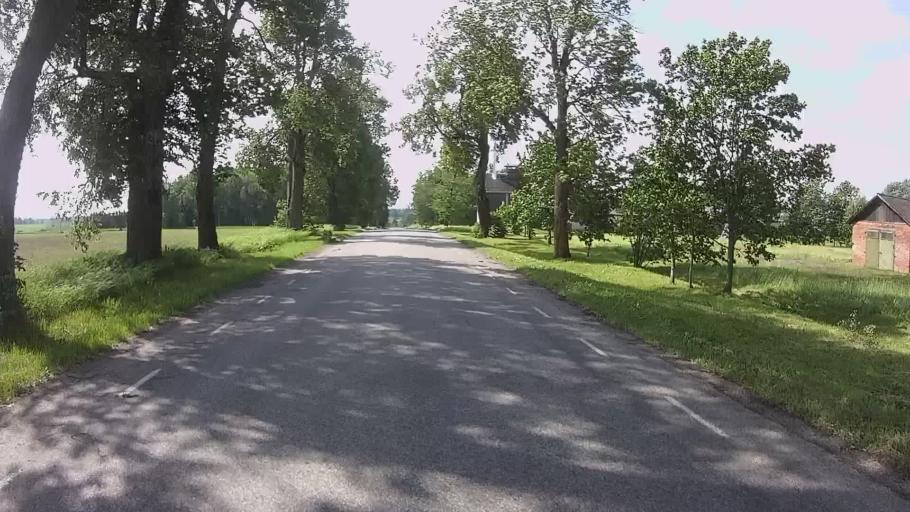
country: EE
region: Vorumaa
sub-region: Antsla vald
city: Vana-Antsla
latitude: 57.8649
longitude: 26.6086
